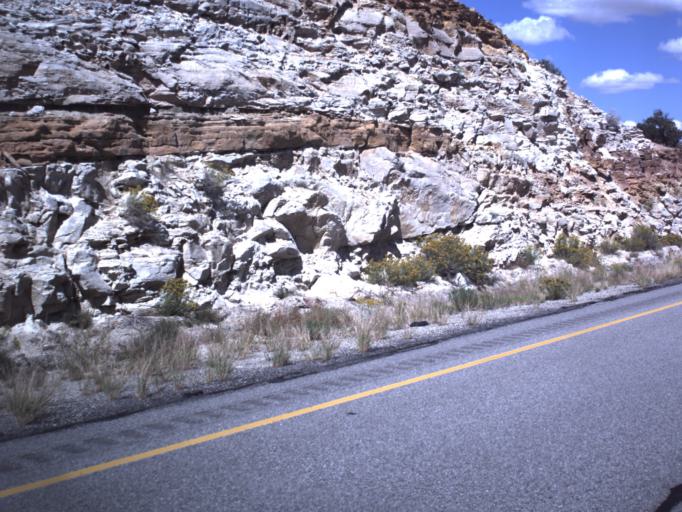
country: US
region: Utah
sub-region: Emery County
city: Ferron
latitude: 38.8484
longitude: -110.8863
